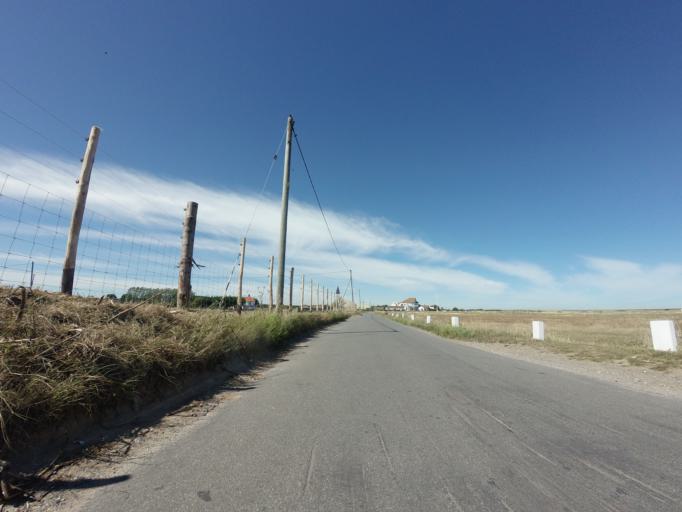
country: GB
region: England
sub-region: Kent
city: Deal
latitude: 51.2372
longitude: 1.3975
